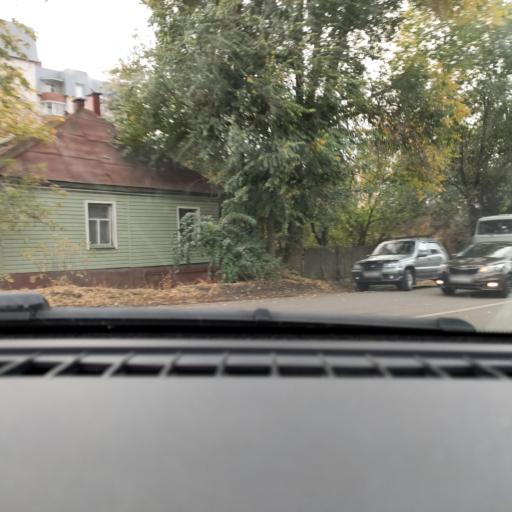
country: RU
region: Voronezj
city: Voronezh
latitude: 51.6456
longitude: 39.1737
